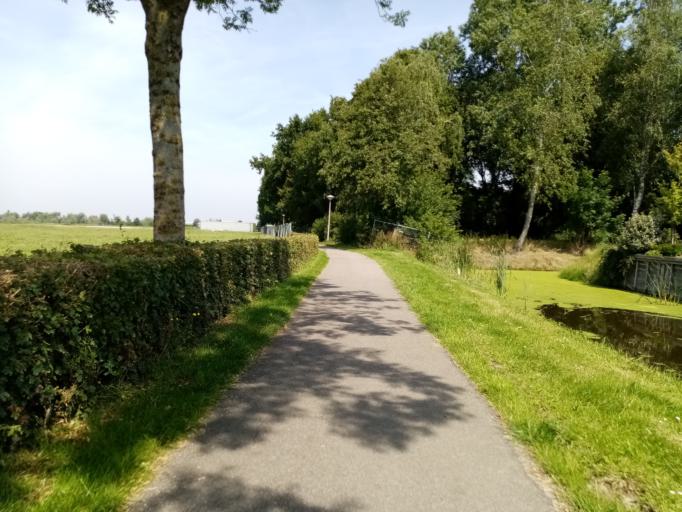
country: NL
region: South Holland
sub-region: Gemeente Nieuwkoop
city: Nieuwkoop
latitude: 52.1986
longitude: 4.7517
